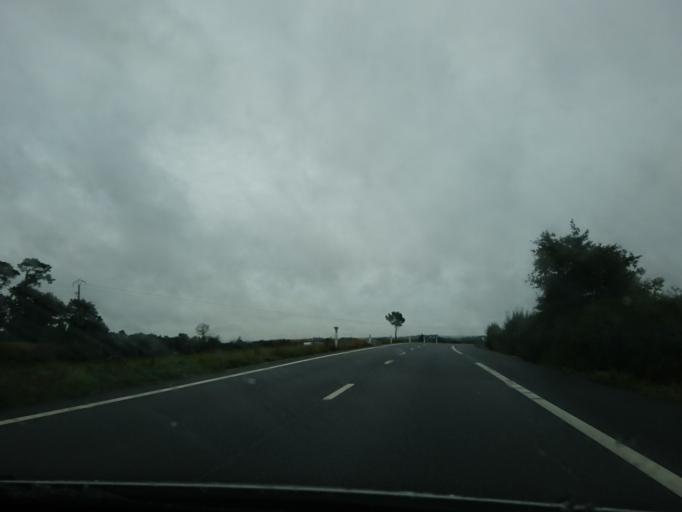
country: FR
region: Brittany
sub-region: Departement du Morbihan
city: Muzillac
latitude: 47.5701
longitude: -2.5175
